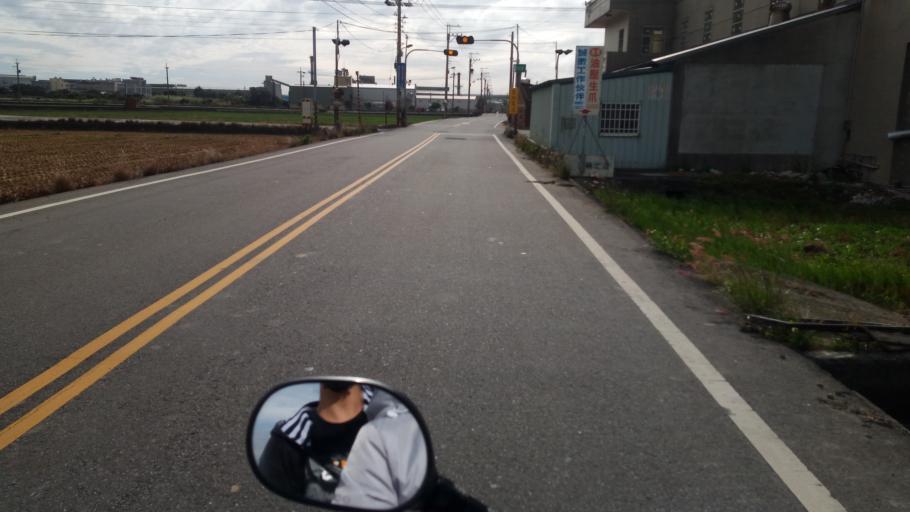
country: TW
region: Taiwan
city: Fengyuan
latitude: 24.4157
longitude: 120.6508
